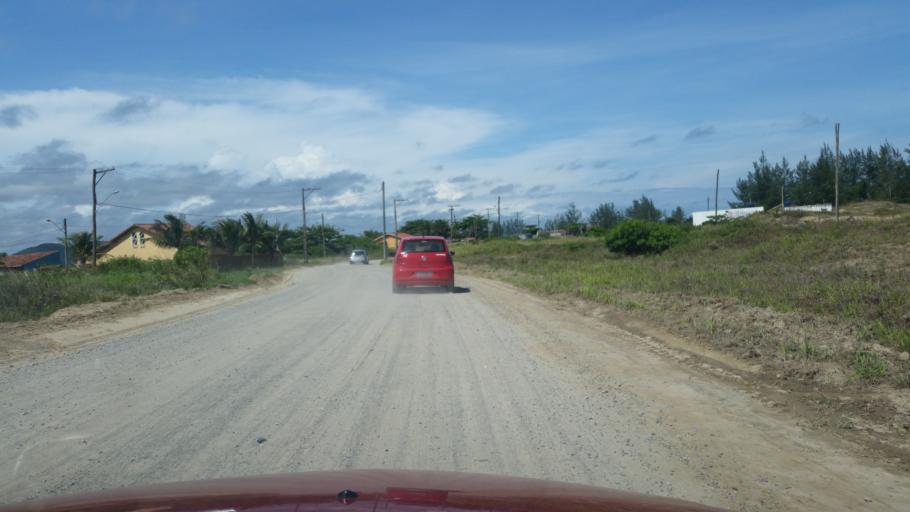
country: BR
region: Sao Paulo
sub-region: Iguape
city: Iguape
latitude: -24.6992
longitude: -47.4583
